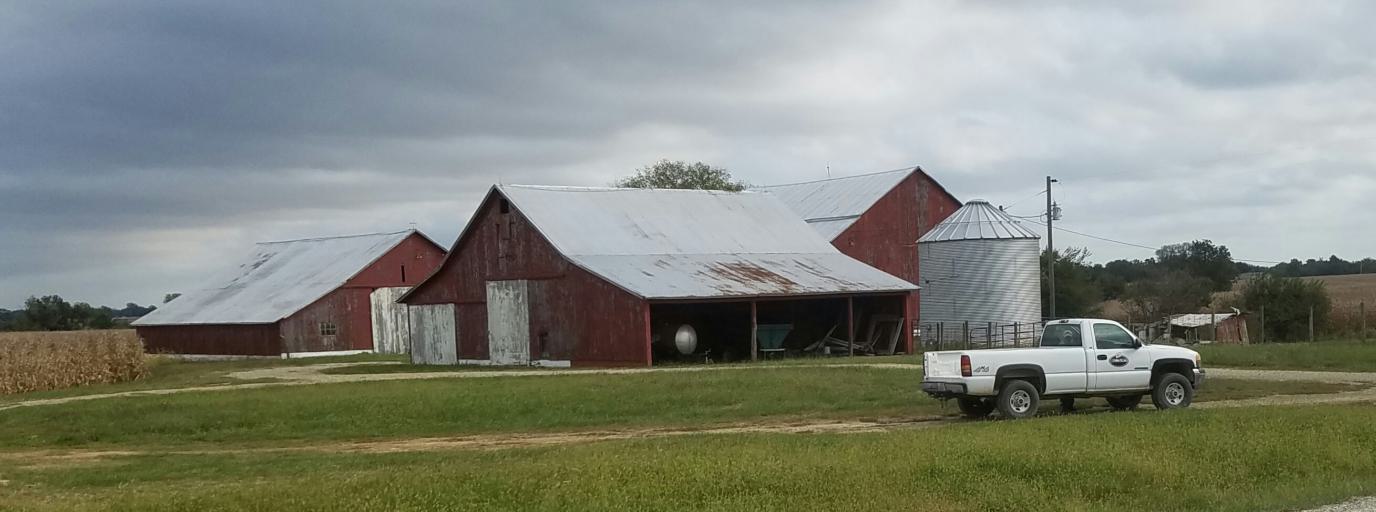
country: US
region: Illinois
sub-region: Fulton County
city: Lewistown
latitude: 40.3371
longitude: -90.1899
